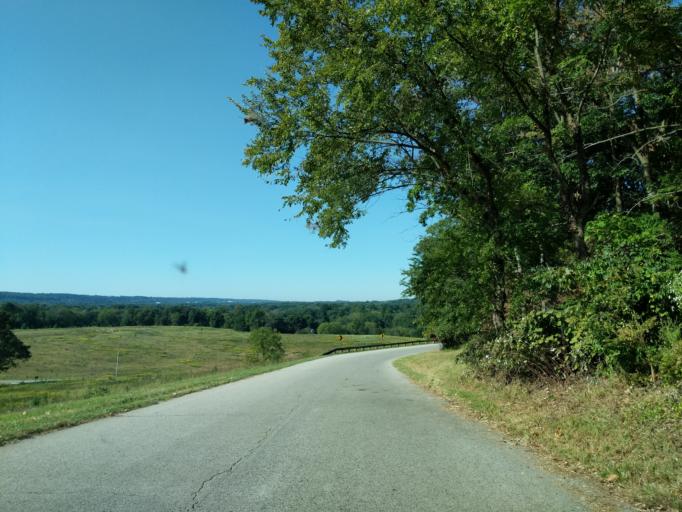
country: US
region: Pennsylvania
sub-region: Chester County
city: Chesterbrook
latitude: 40.0864
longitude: -75.4452
